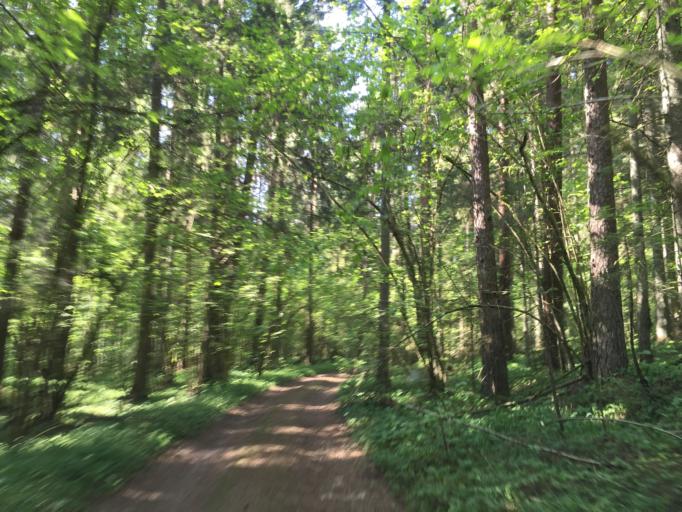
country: LV
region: Baldone
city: Baldone
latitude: 56.7988
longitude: 24.3733
